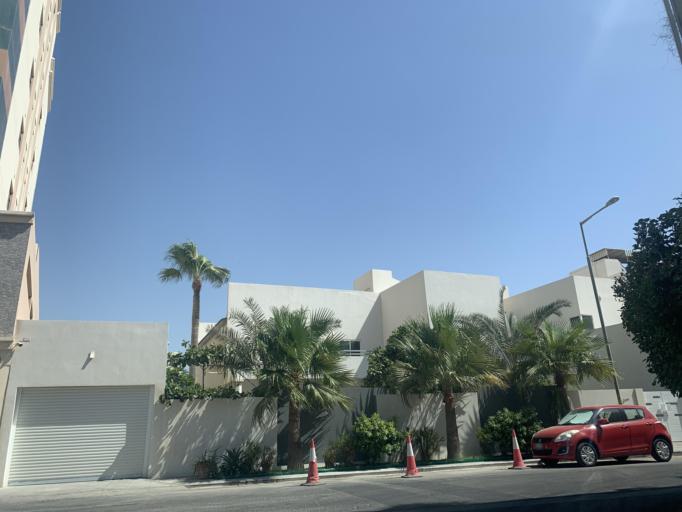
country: BH
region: Manama
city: Jidd Hafs
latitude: 26.2224
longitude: 50.5019
